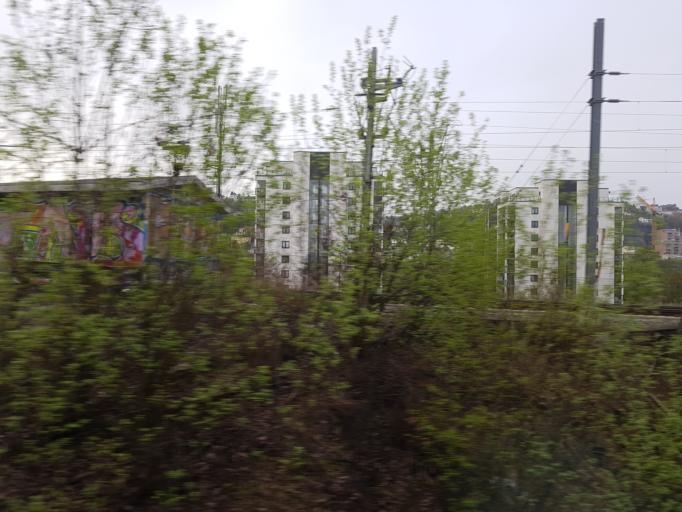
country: NO
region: Oslo
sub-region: Oslo
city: Oslo
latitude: 59.9070
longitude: 10.7989
